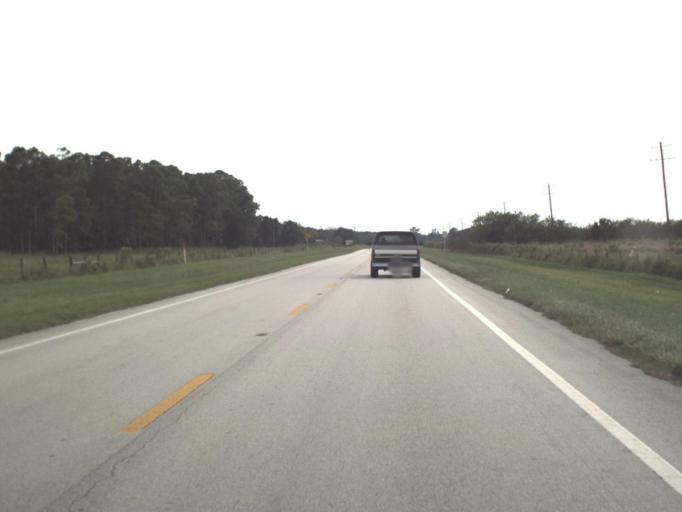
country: US
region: Florida
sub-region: Okeechobee County
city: Cypress Quarters
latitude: 27.3134
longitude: -80.8256
